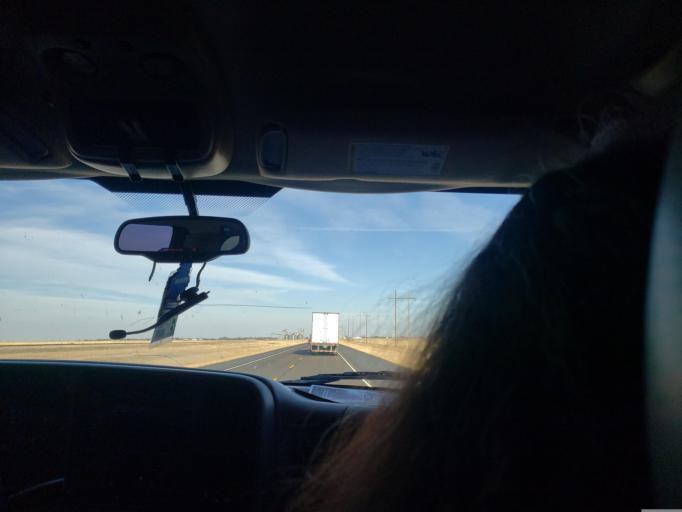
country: US
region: Oklahoma
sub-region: Texas County
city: Goodwell
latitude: 36.4847
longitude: -101.8134
